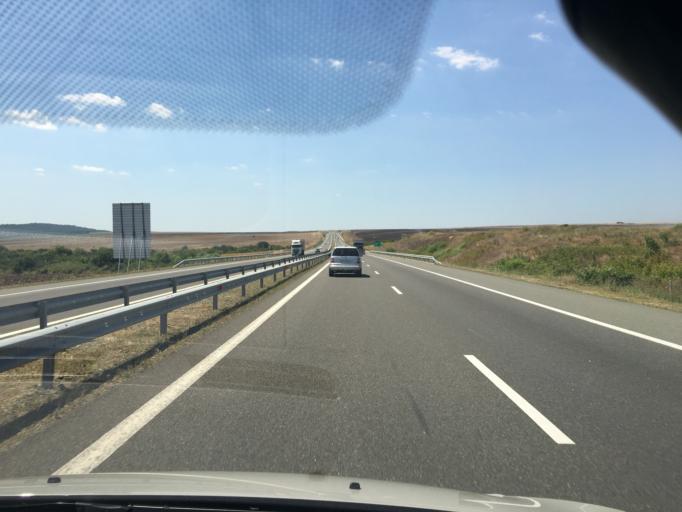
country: BG
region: Burgas
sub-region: Obshtina Karnobat
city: Karnobat
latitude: 42.5902
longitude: 26.9764
